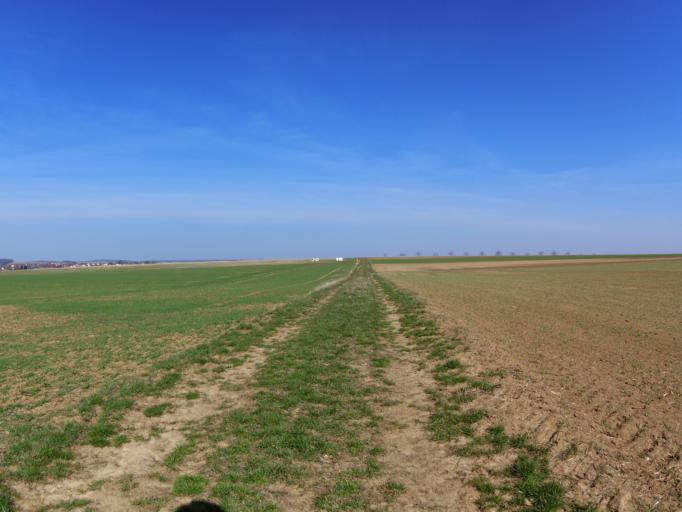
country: DE
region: Bavaria
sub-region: Regierungsbezirk Unterfranken
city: Estenfeld
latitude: 49.8148
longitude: 10.0150
